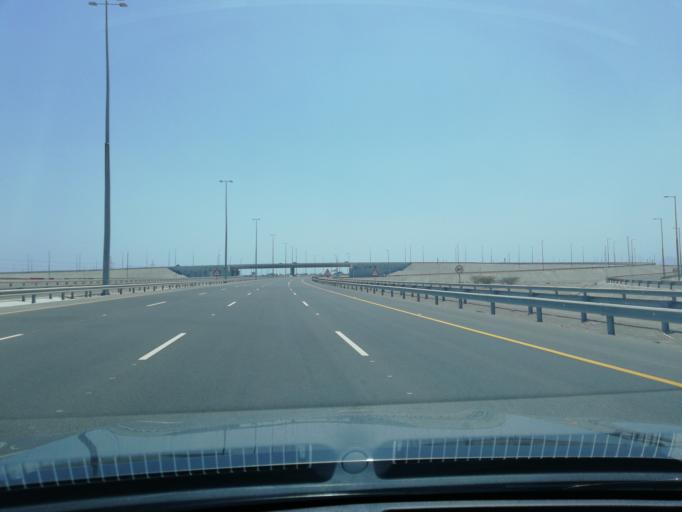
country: OM
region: Al Batinah
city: Barka'
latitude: 23.6331
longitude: 57.8687
